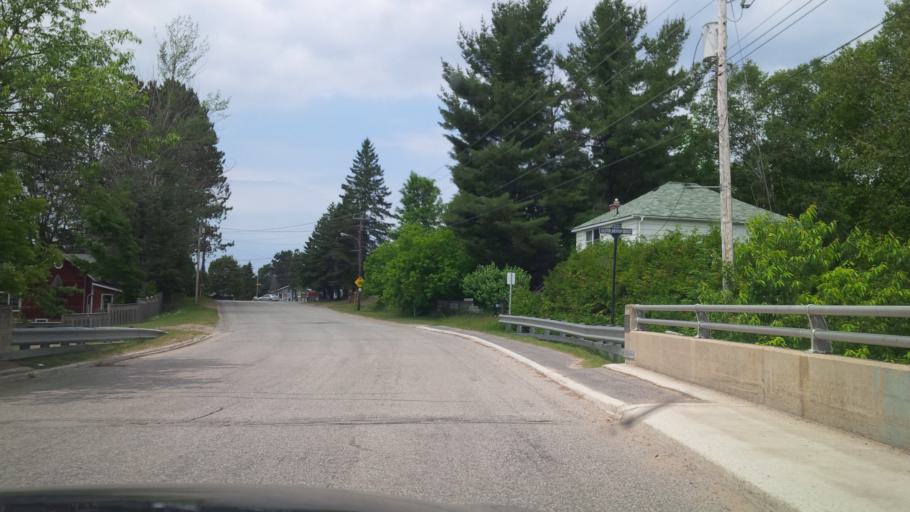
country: CA
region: Ontario
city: Huntsville
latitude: 45.5573
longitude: -79.2254
